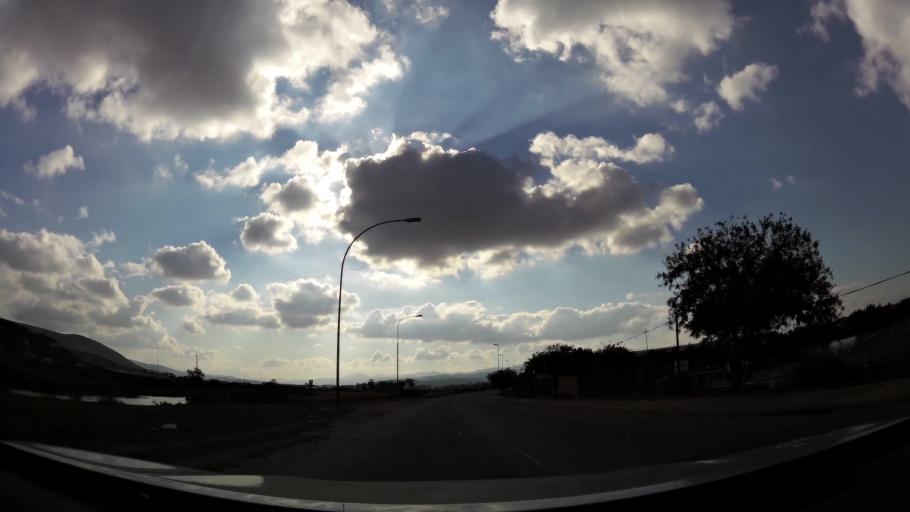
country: ZA
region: Eastern Cape
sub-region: Nelson Mandela Bay Metropolitan Municipality
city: Uitenhage
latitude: -33.7796
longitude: 25.3934
